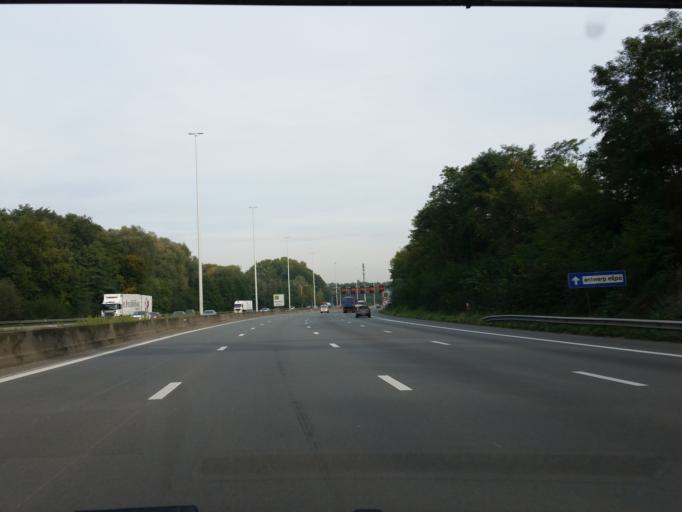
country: BE
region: Flanders
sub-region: Provincie Antwerpen
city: Edegem
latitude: 51.1641
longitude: 4.4139
